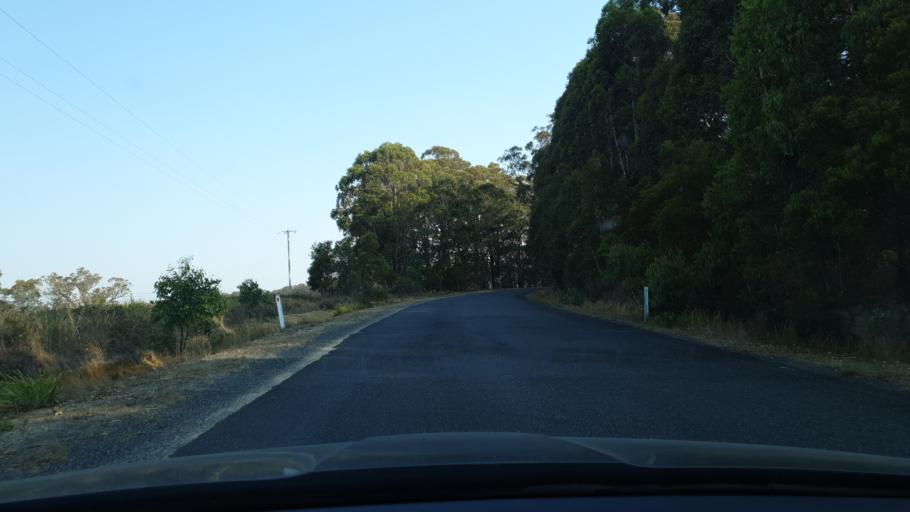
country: AU
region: New South Wales
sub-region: Tenterfield Municipality
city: Carrolls Creek
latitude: -28.6921
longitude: 152.0895
